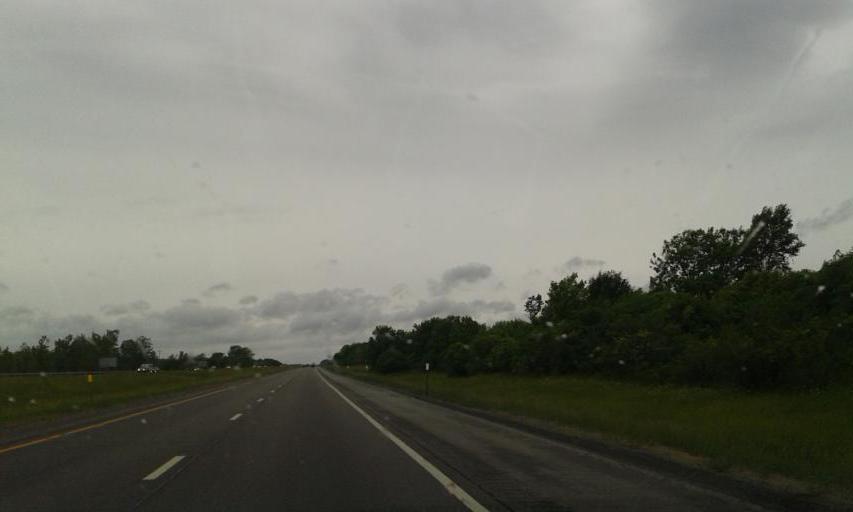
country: US
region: New York
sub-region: Genesee County
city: Batavia
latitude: 43.0184
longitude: -78.1955
